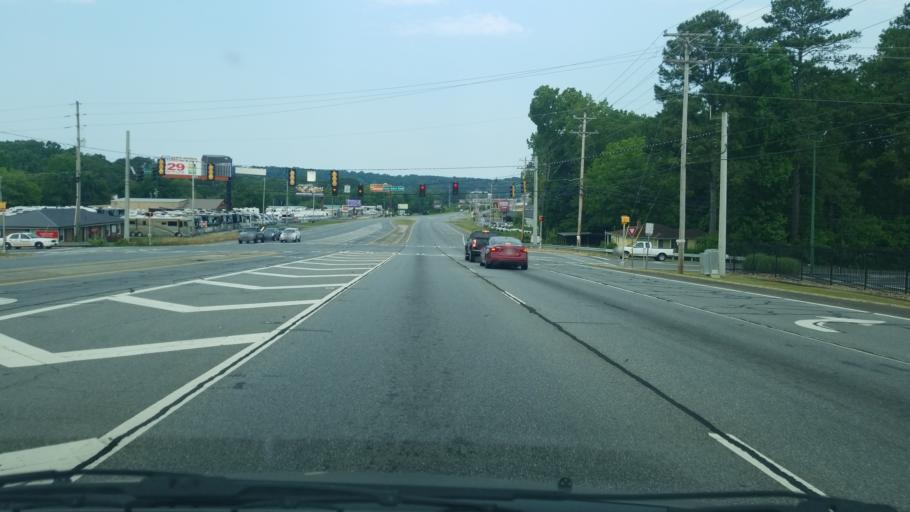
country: US
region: Georgia
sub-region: Catoosa County
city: Indian Springs
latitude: 34.9300
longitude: -85.1712
